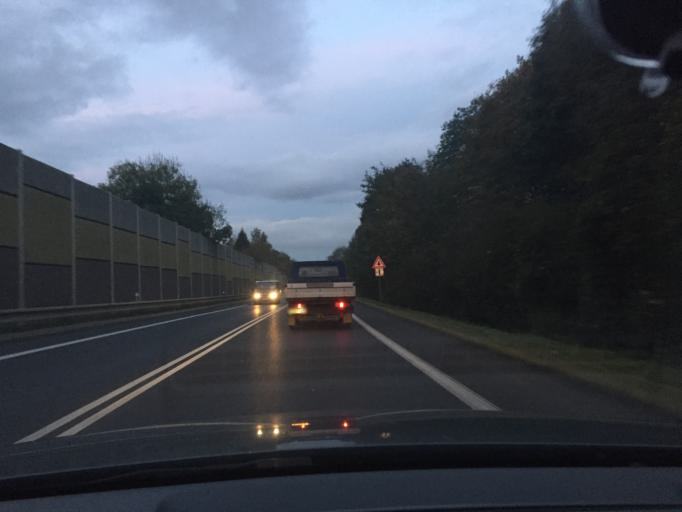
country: CZ
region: Ustecky
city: Bystrany
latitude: 50.6285
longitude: 13.8602
